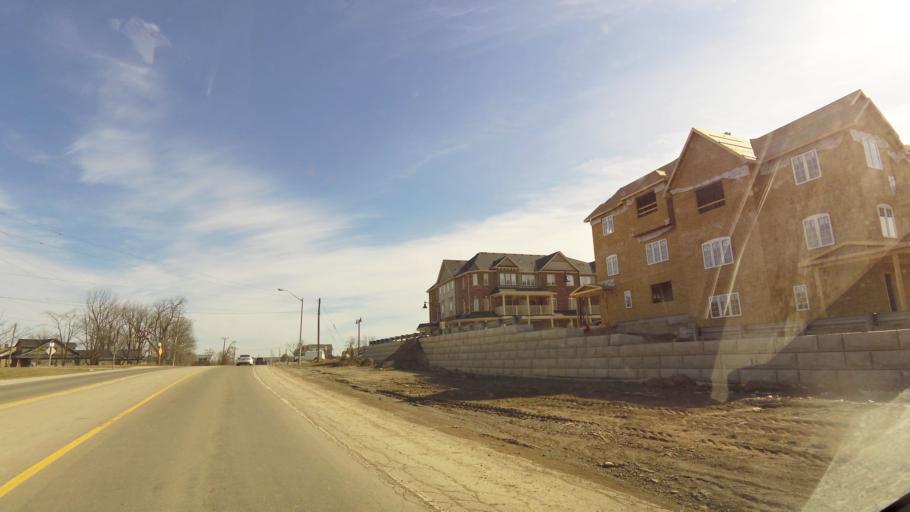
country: CA
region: Ontario
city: Burlington
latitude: 43.3394
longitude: -79.9066
